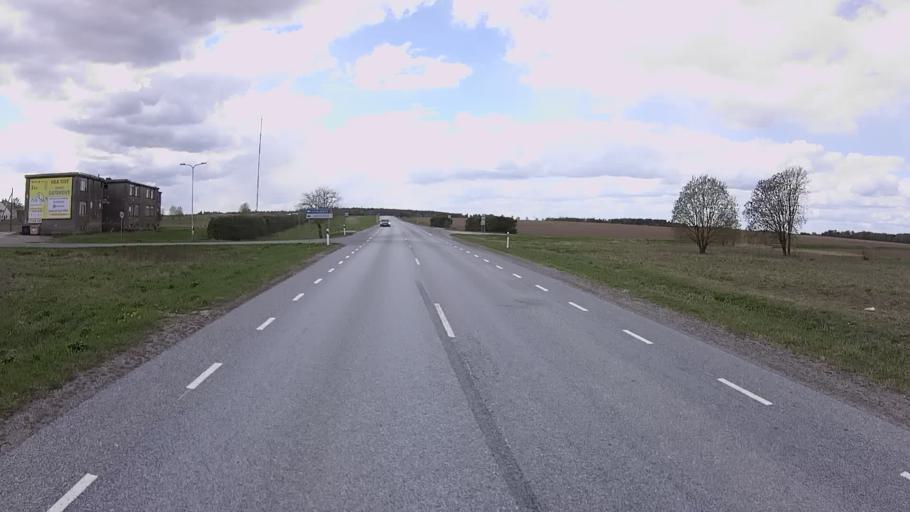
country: EE
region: Jaervamaa
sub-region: Koeru vald
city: Koeru
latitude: 58.9791
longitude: 26.0869
